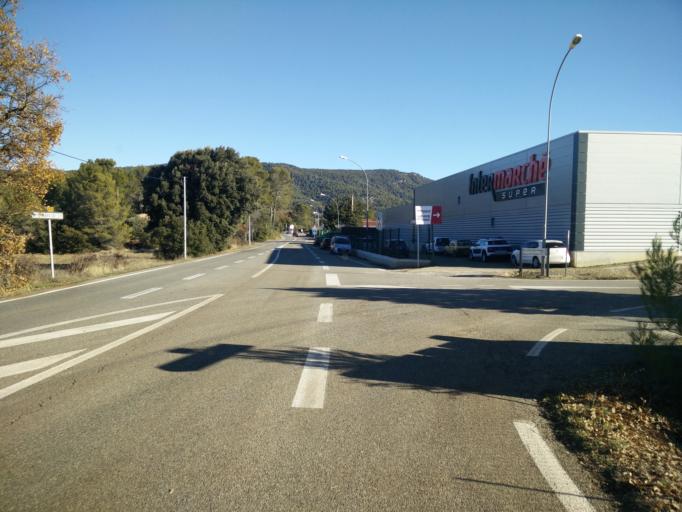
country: FR
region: Provence-Alpes-Cote d'Azur
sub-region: Departement du Var
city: Aups
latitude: 43.6166
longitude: 6.2180
